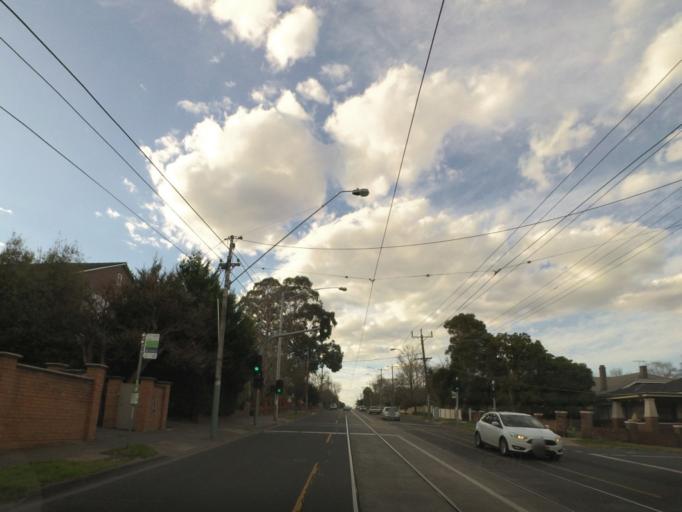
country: AU
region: Victoria
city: Glenferrie
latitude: -37.8404
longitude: 145.0549
